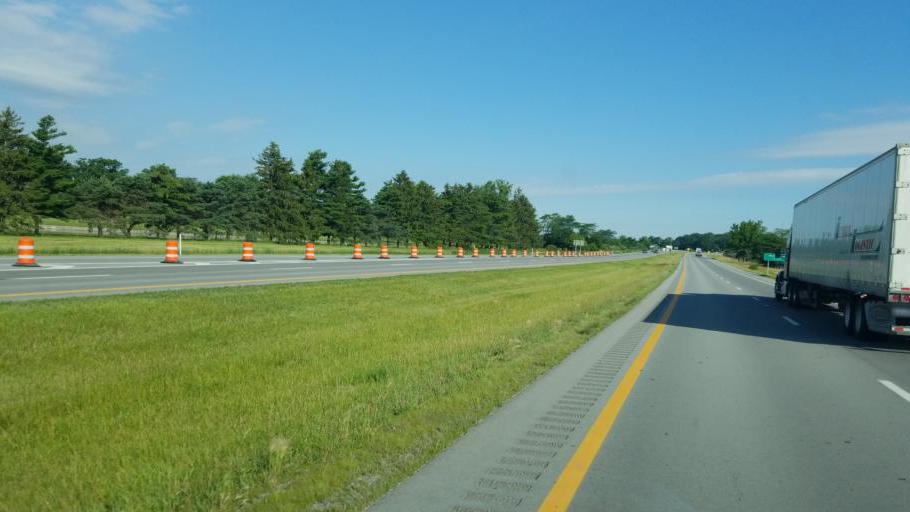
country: US
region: Ohio
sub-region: Hancock County
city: Findlay
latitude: 40.9968
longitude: -83.6533
